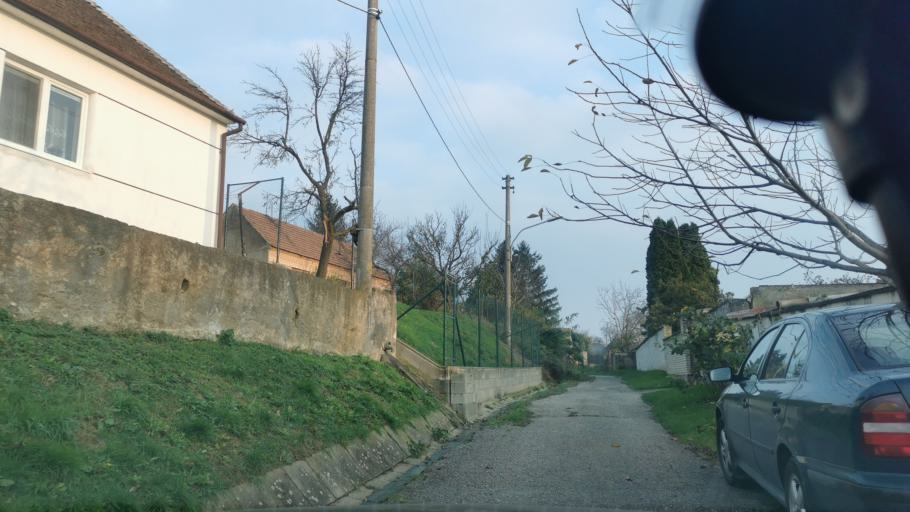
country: SK
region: Trnavsky
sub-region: Okres Skalica
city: Skalica
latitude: 48.7891
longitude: 17.2178
